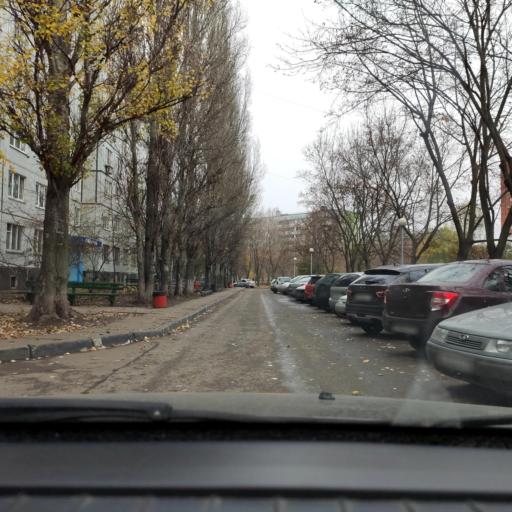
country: RU
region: Samara
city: Tol'yatti
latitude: 53.5274
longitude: 49.3237
